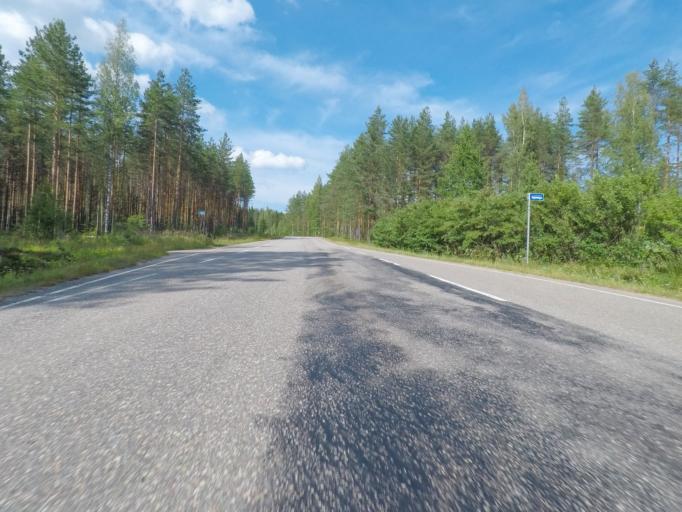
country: FI
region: Southern Savonia
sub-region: Mikkeli
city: Puumala
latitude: 61.6803
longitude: 28.2302
